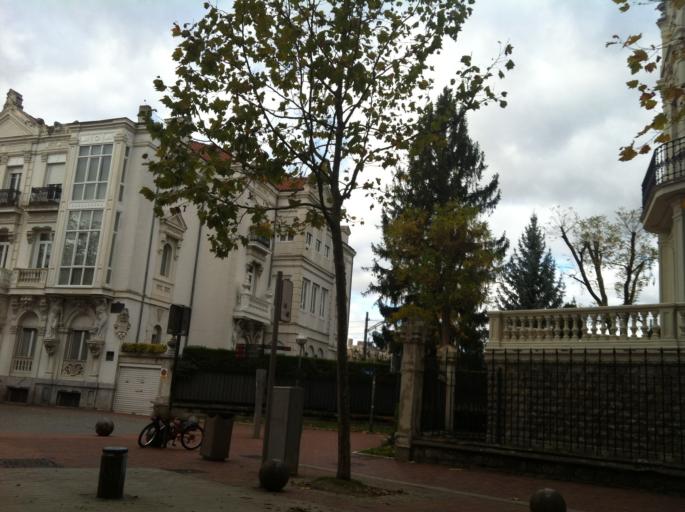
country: ES
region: Basque Country
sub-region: Provincia de Alava
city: Gasteiz / Vitoria
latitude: 42.8415
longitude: -2.6782
